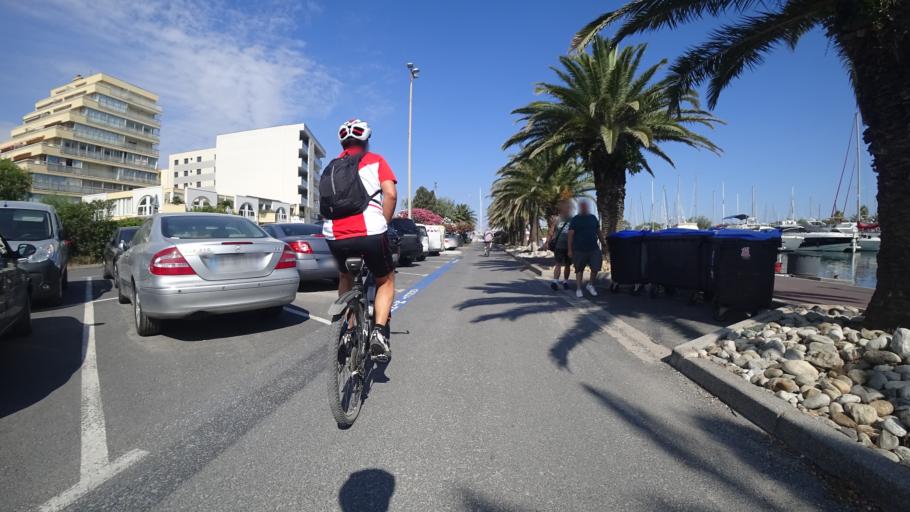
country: FR
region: Languedoc-Roussillon
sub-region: Departement des Pyrenees-Orientales
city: Canet-en-Roussillon
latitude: 42.7025
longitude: 3.0349
